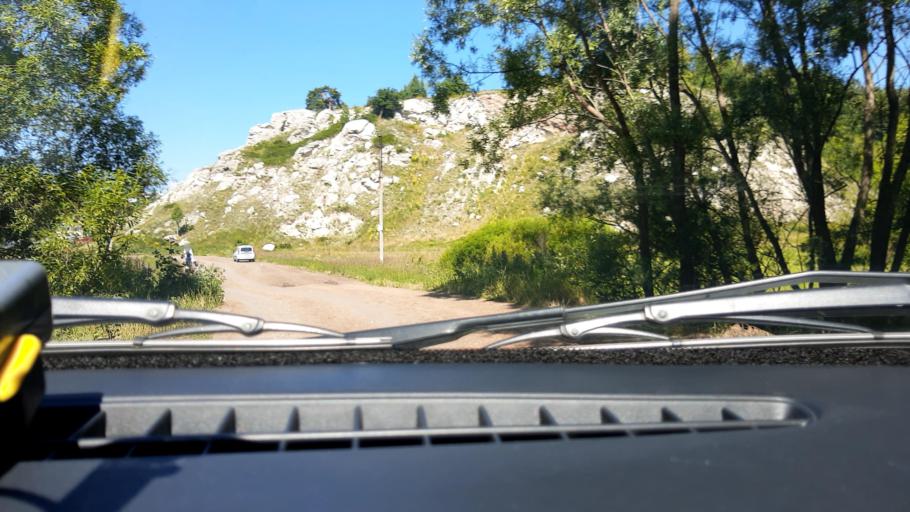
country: RU
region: Bashkortostan
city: Karmaskaly
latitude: 54.3589
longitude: 55.9020
